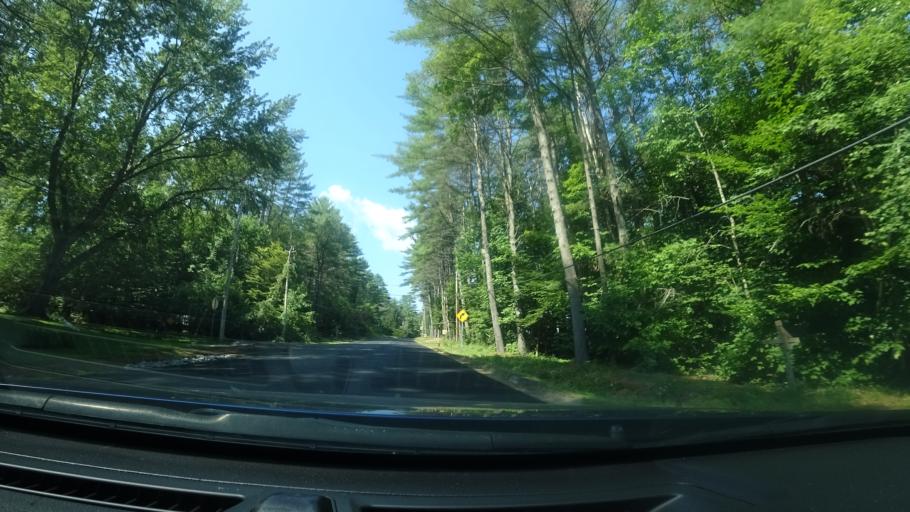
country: US
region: New York
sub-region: Warren County
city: Warrensburg
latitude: 43.6528
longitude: -73.8092
